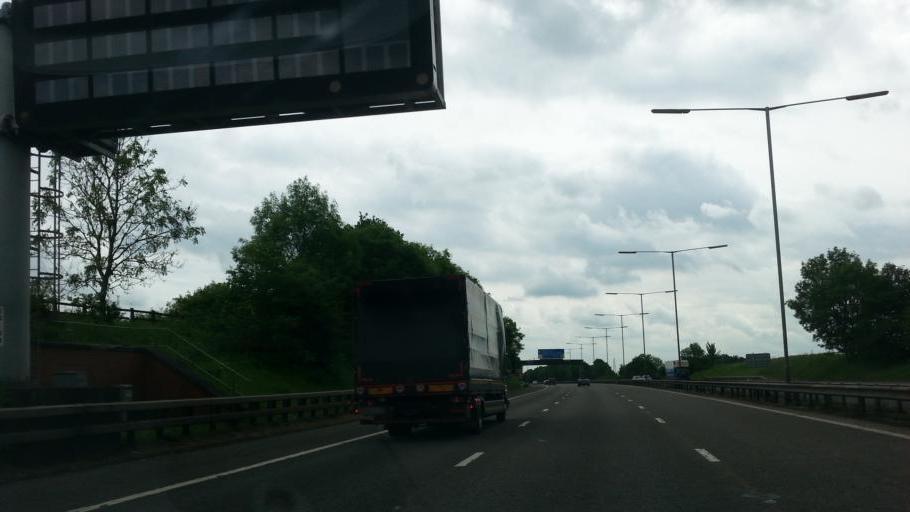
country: GB
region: England
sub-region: Warwickshire
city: Bedworth
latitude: 52.4512
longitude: -1.4225
